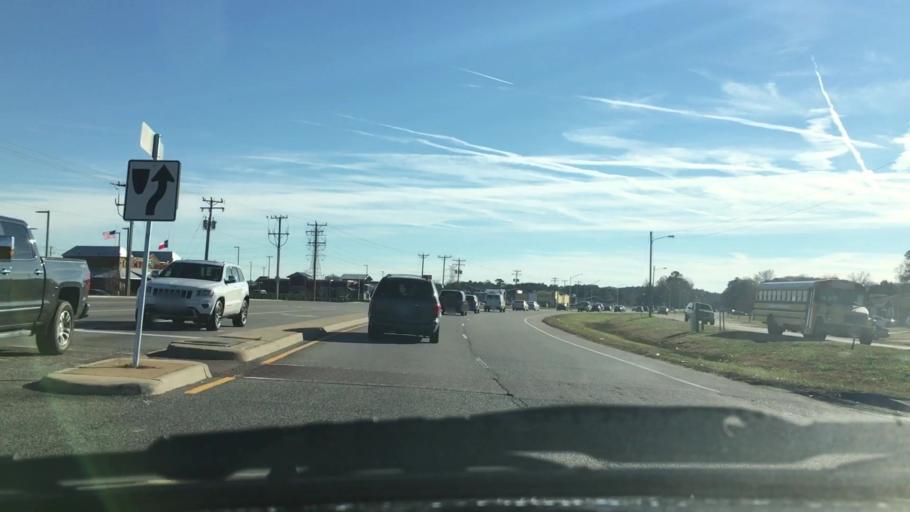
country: US
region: Virginia
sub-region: City of Portsmouth
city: Portsmouth Heights
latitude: 36.8775
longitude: -76.4233
